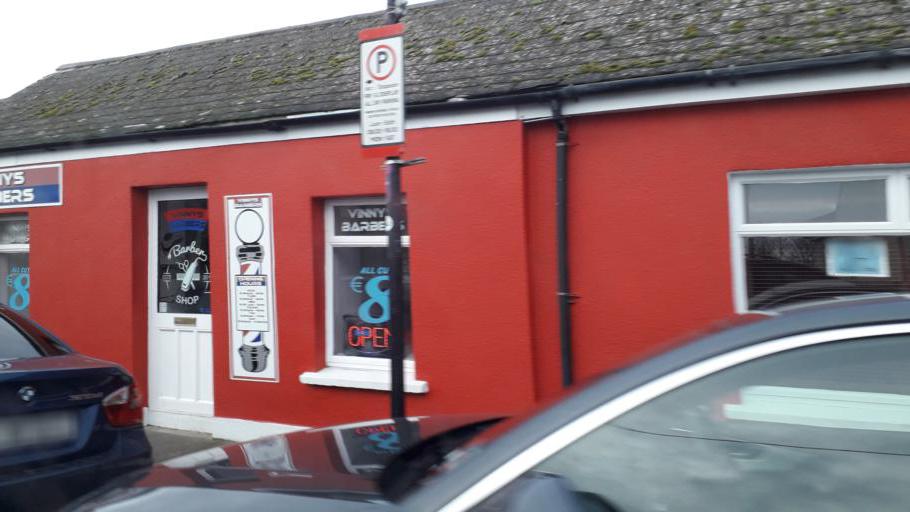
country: IE
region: Leinster
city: An Ros
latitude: 53.5225
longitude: -6.0974
